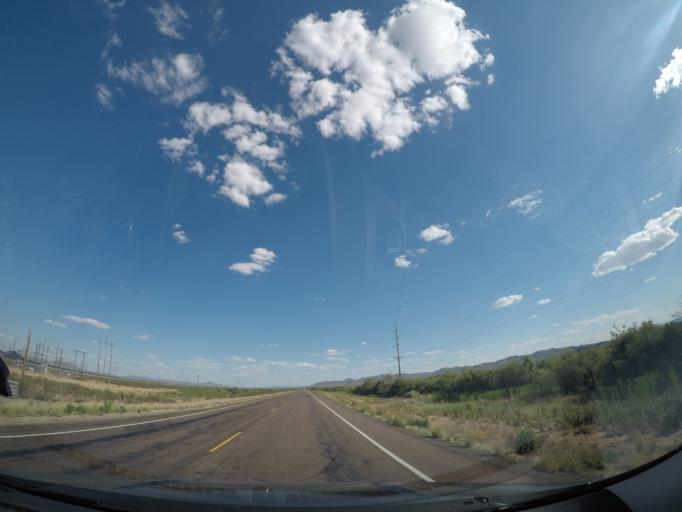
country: US
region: Texas
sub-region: Culberson County
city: Van Horn
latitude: 30.9851
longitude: -104.8209
